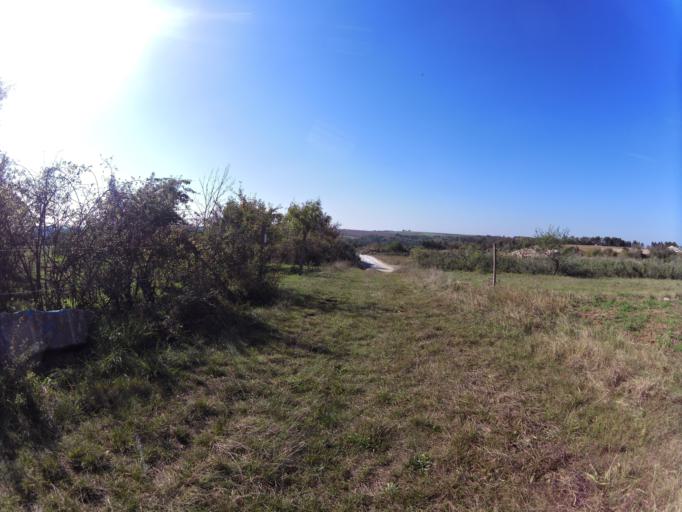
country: DE
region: Bavaria
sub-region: Regierungsbezirk Unterfranken
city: Sommerhausen
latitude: 49.6863
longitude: 10.0386
